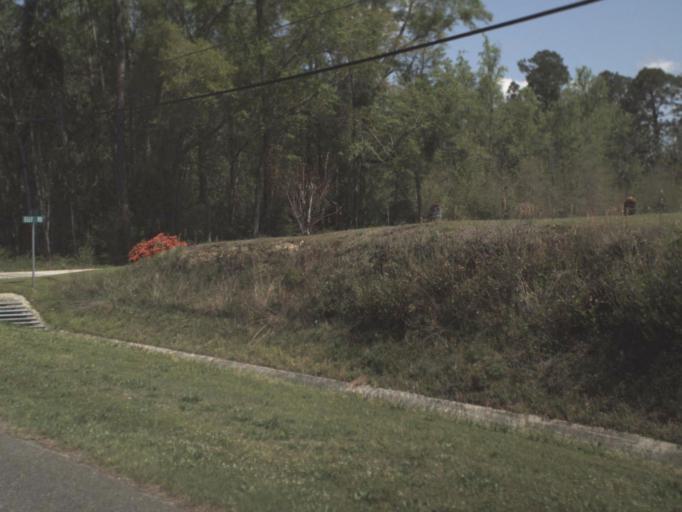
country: US
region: Alabama
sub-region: Escambia County
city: East Brewton
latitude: 30.9202
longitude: -87.0474
